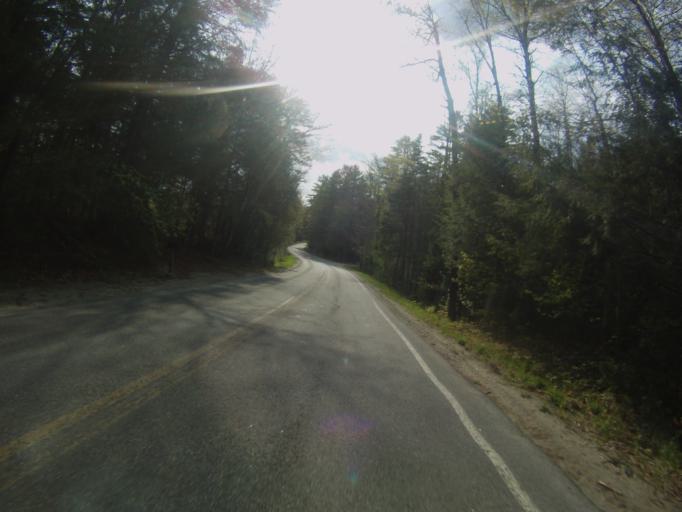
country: US
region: New York
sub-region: Warren County
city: Warrensburg
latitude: 43.8454
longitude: -73.8031
